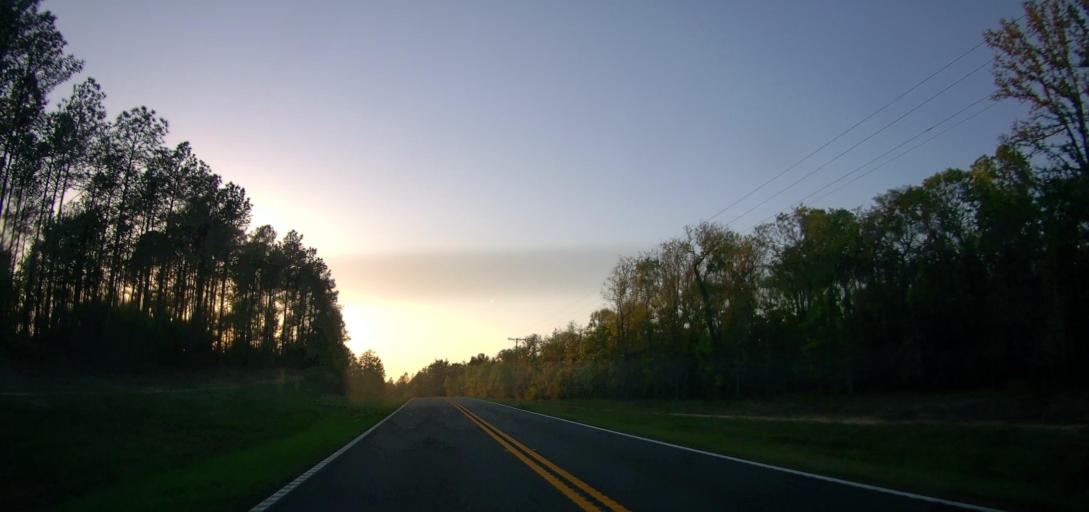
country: US
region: Georgia
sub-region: Marion County
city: Buena Vista
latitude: 32.4404
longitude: -84.6026
